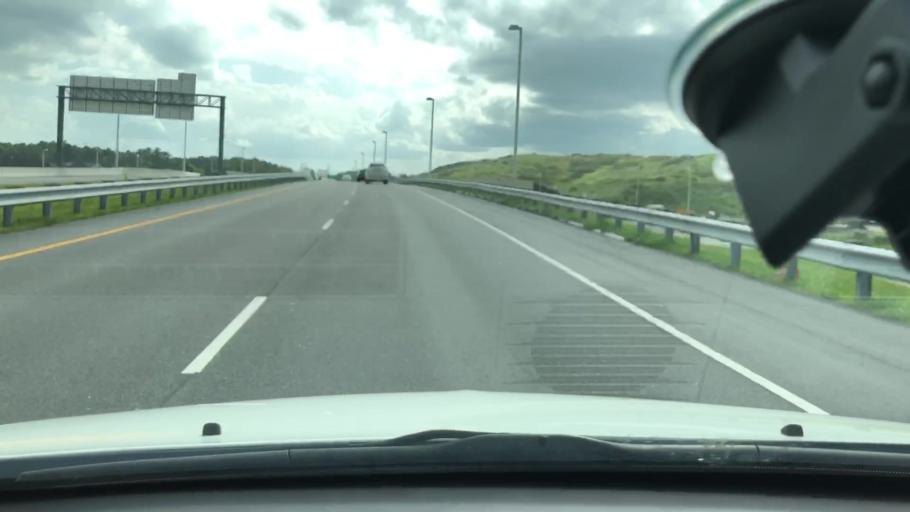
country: US
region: Virginia
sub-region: City of Chesapeake
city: Chesapeake
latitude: 36.7486
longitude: -76.2838
